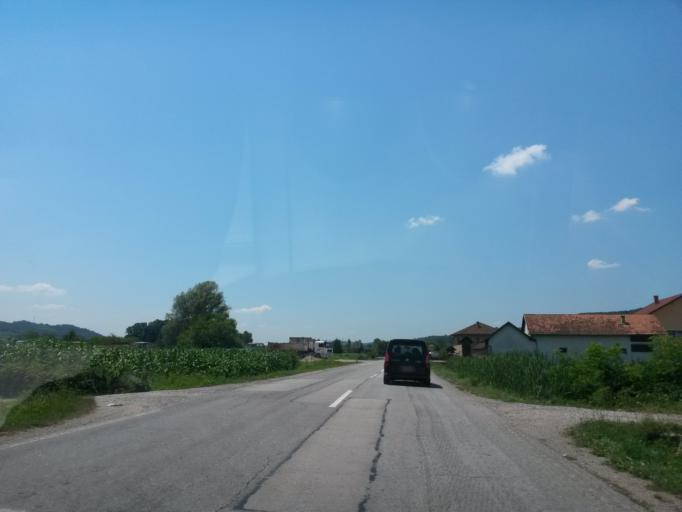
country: BA
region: Federation of Bosnia and Herzegovina
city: Lukavica
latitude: 44.9318
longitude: 18.1129
